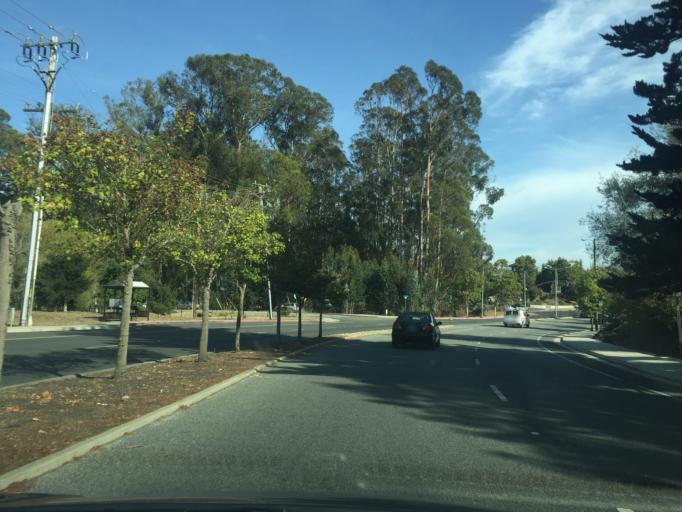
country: US
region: California
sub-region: Santa Cruz County
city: Seacliff
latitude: 36.9905
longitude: -121.9305
